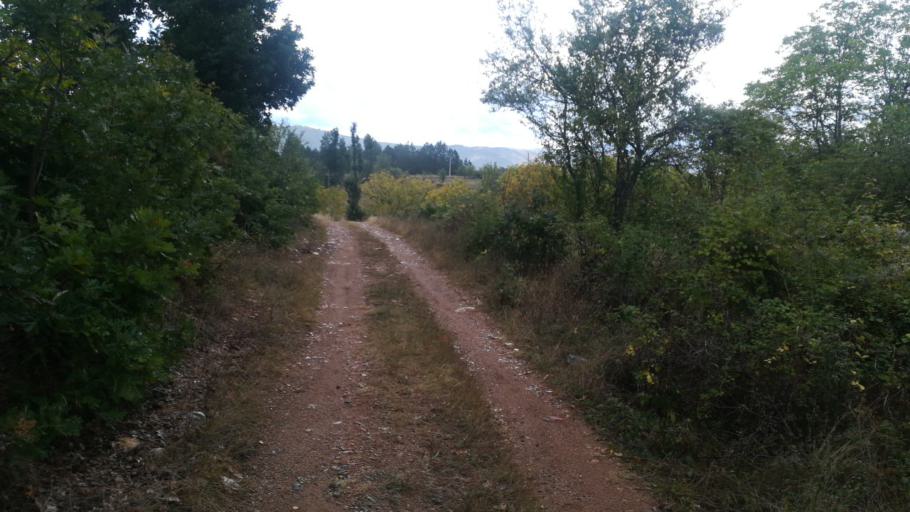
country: MK
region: Makedonska Kamenica
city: Makedonska Kamenica
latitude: 42.0169
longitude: 22.5748
